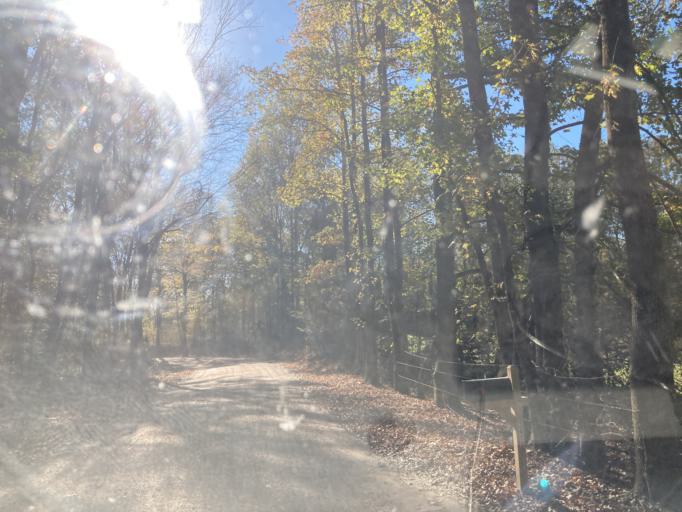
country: US
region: Mississippi
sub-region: Yazoo County
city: Yazoo City
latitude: 32.7551
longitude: -90.3891
